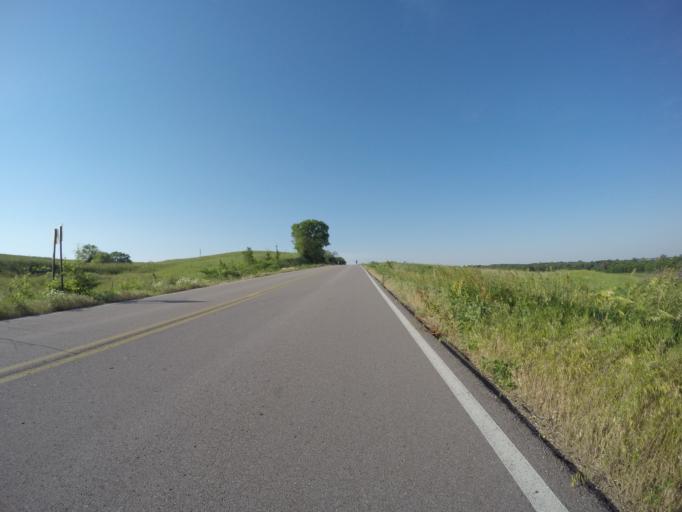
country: US
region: Nebraska
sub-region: Gage County
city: Wymore
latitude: 40.1013
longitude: -96.5016
